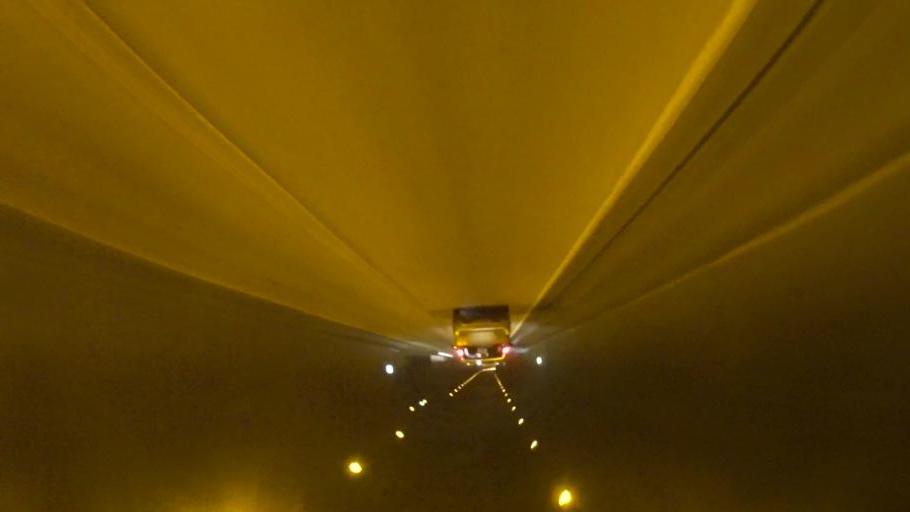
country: JP
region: Kyoto
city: Miyazu
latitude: 35.5487
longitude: 135.1775
